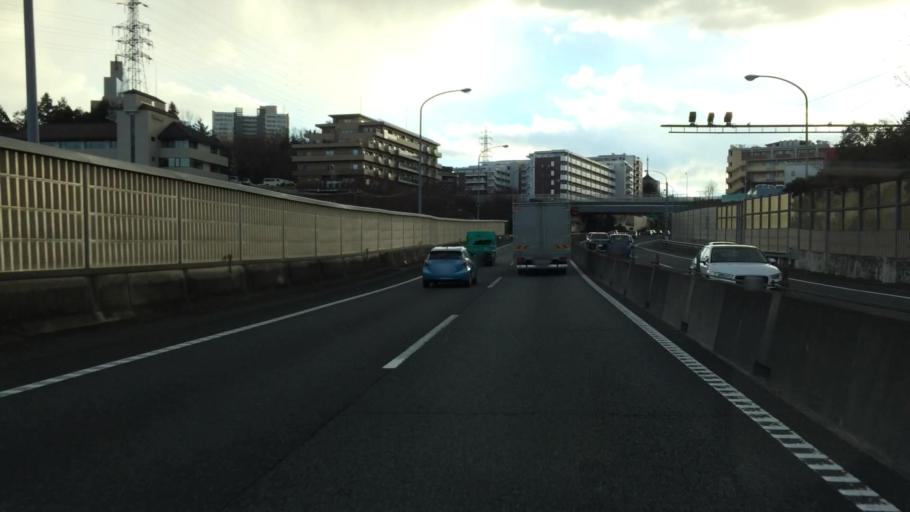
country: JP
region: Kanagawa
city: Yokohama
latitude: 35.4359
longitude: 139.5549
